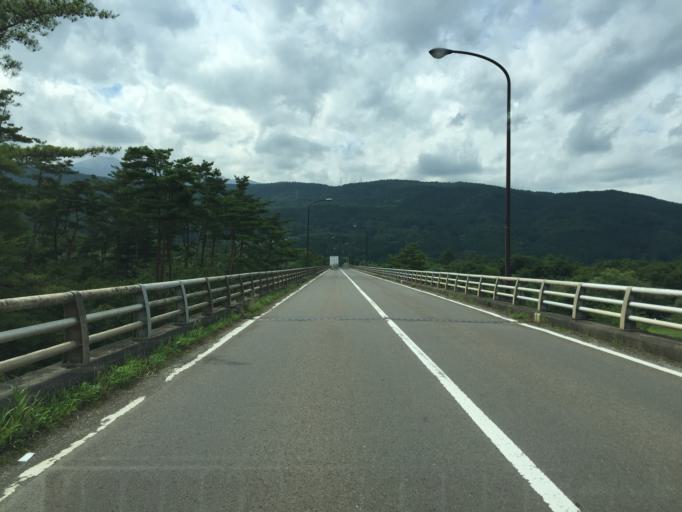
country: JP
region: Fukushima
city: Fukushima-shi
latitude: 37.7092
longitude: 140.3580
